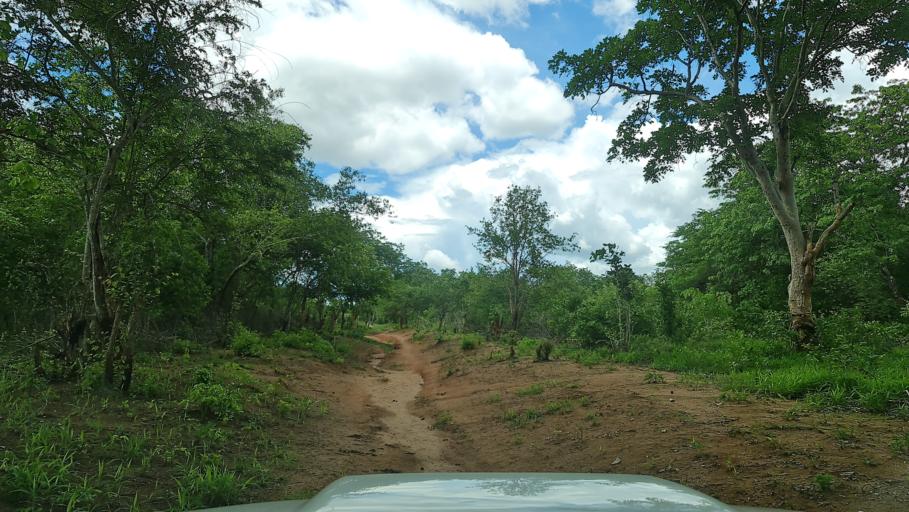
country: MZ
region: Nampula
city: Ilha de Mocambique
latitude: -15.5048
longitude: 40.1872
